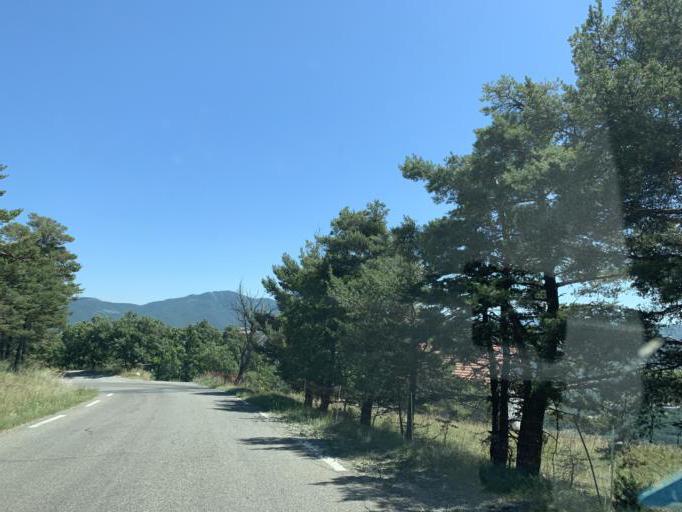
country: FR
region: Provence-Alpes-Cote d'Azur
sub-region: Departement des Hautes-Alpes
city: La Batie-Neuve
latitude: 44.5888
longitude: 6.1571
